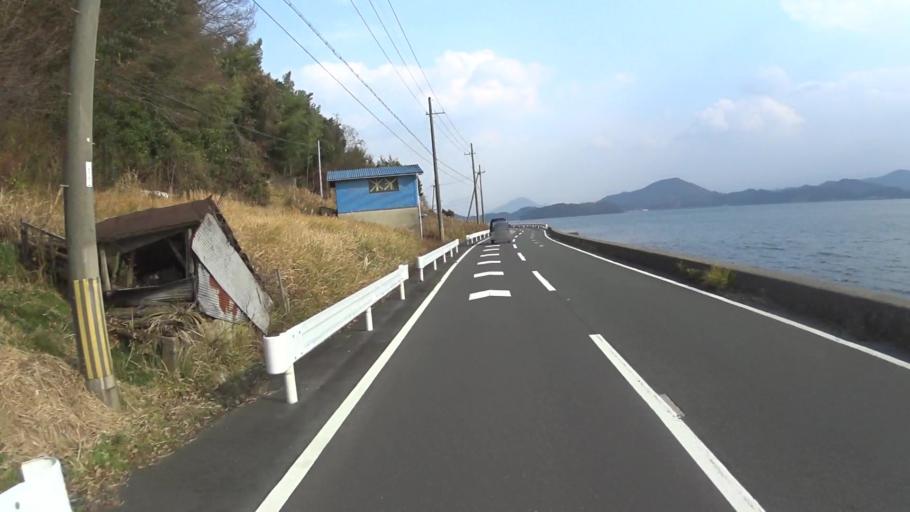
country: JP
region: Kyoto
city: Maizuru
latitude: 35.4905
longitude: 135.3262
